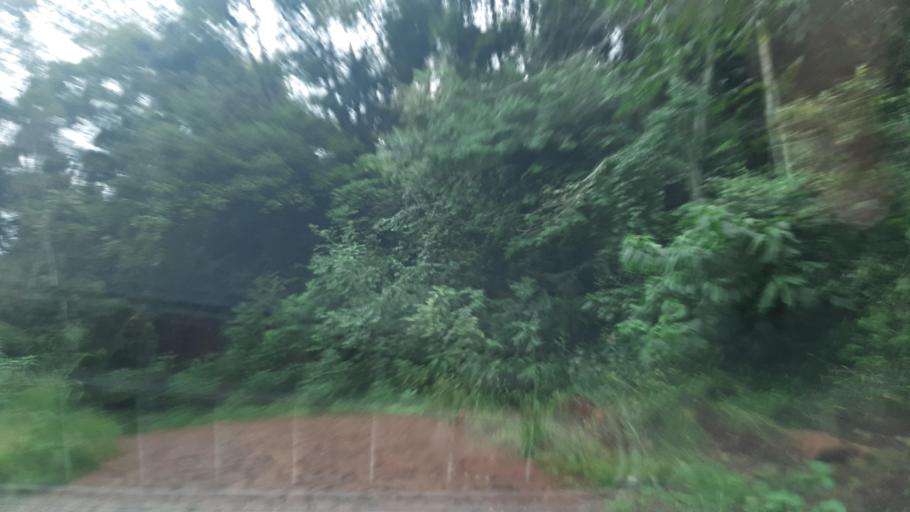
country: BR
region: Parana
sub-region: Ampere
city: Ampere
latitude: -26.0397
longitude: -53.5135
